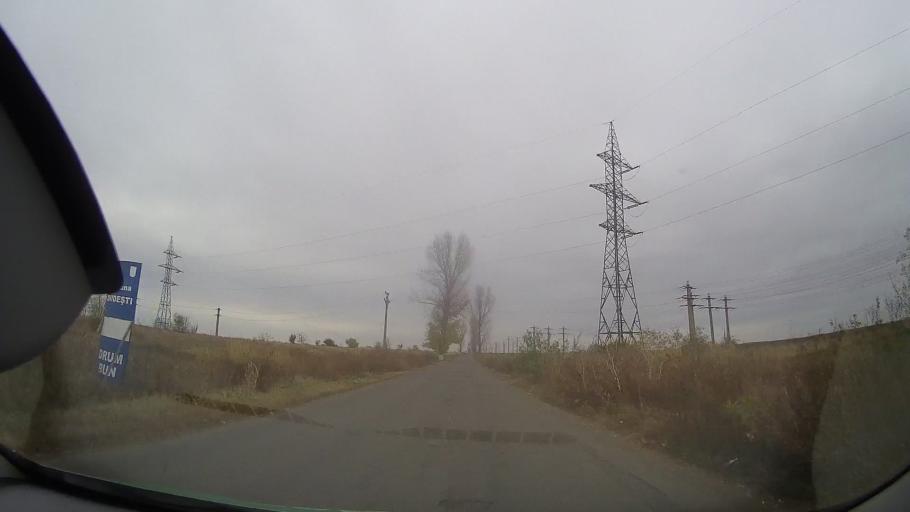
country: RO
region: Braila
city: Dudesti
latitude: 44.8979
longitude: 27.4330
